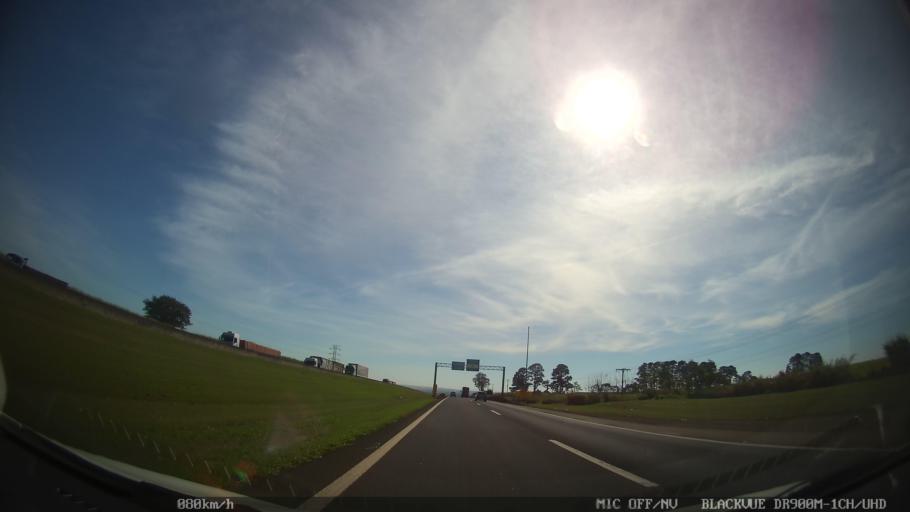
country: BR
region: Sao Paulo
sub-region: Leme
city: Leme
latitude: -22.2627
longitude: -47.3906
